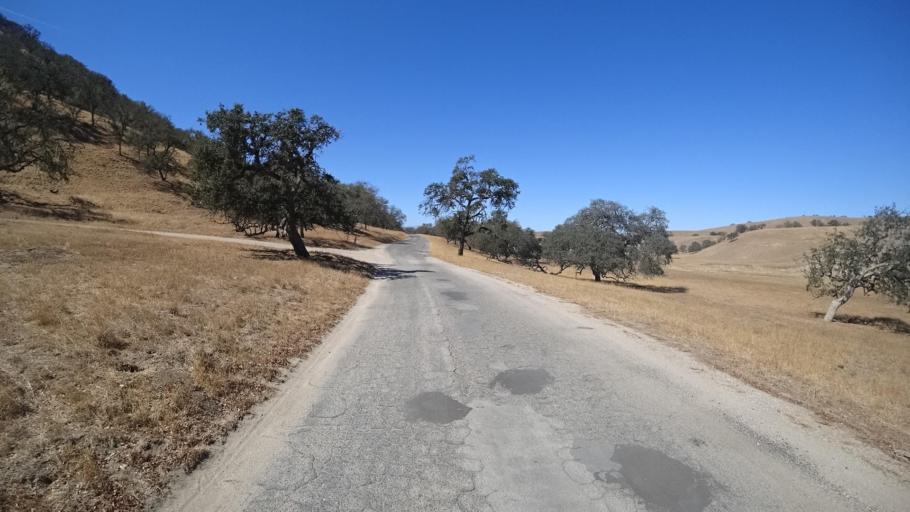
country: US
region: California
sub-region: San Luis Obispo County
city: Lake Nacimiento
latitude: 35.9514
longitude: -120.8191
